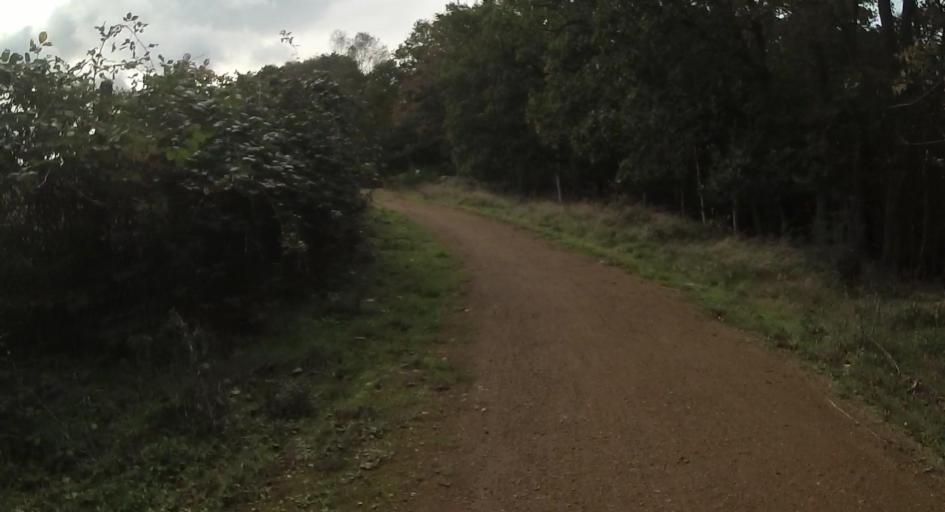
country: GB
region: England
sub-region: Surrey
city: Frimley
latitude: 51.3081
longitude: -0.6973
